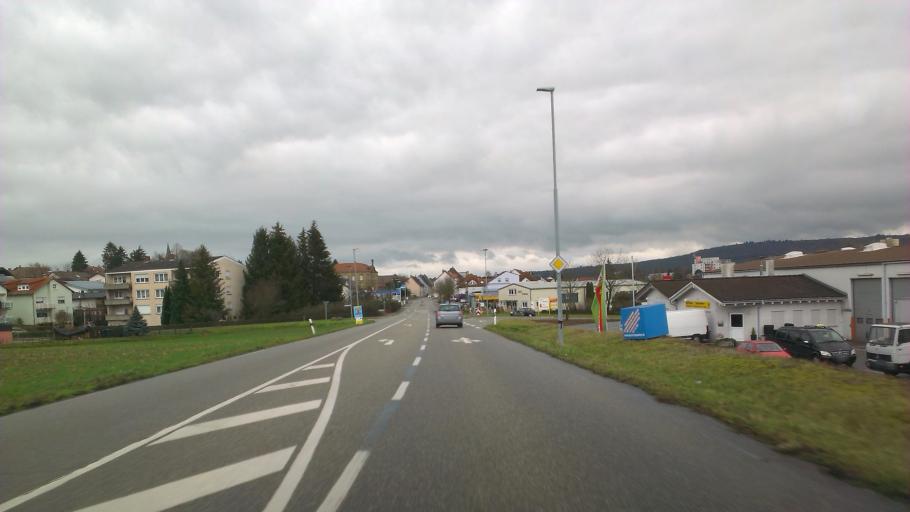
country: DE
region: Baden-Wuerttemberg
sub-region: Regierungsbezirk Stuttgart
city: Eppingen
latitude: 49.1343
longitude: 8.8979
